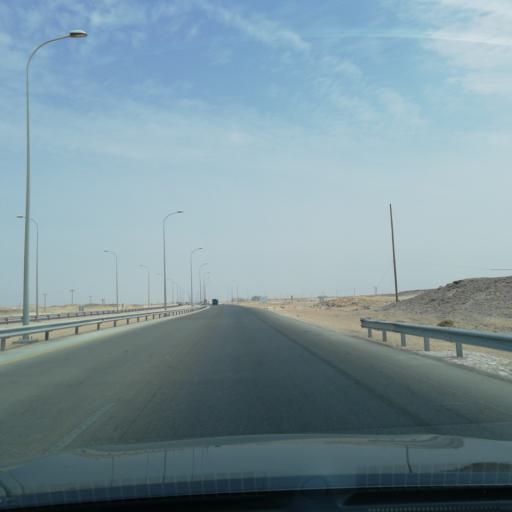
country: OM
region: Zufar
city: Salalah
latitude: 17.5898
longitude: 54.0403
